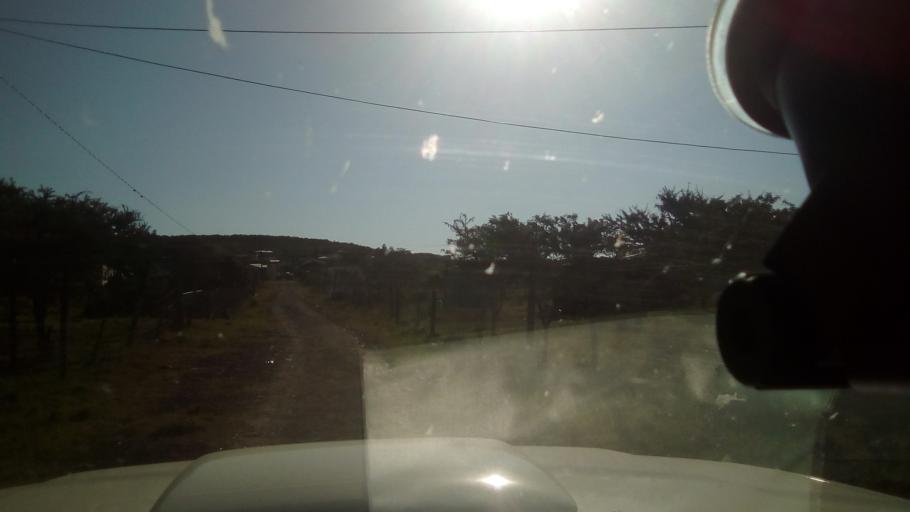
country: ZA
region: Eastern Cape
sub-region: Buffalo City Metropolitan Municipality
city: Bhisho
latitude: -32.8128
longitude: 27.3582
